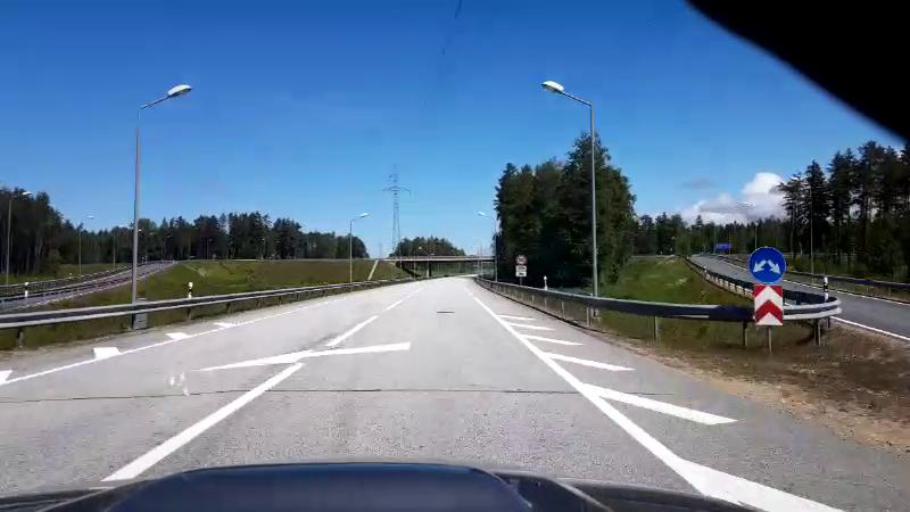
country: LV
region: Saulkrastu
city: Saulkrasti
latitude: 57.2454
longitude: 24.4273
